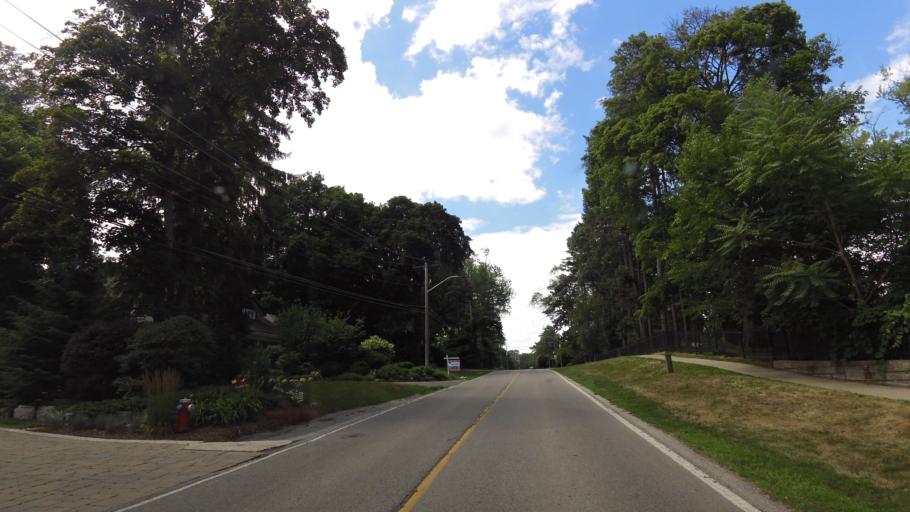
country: CA
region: Ontario
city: Mississauga
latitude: 43.5169
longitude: -79.6181
